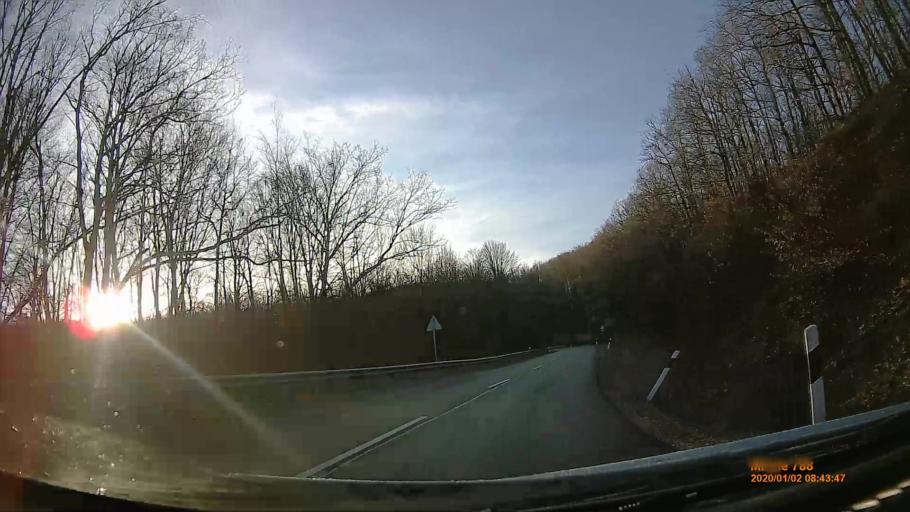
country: HU
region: Heves
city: Paradsasvar
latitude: 47.9075
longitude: 19.9924
